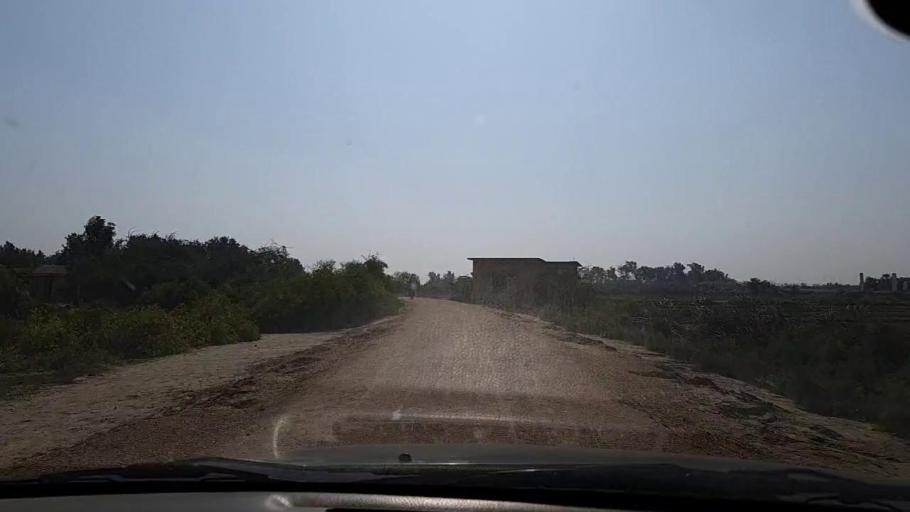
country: PK
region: Sindh
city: Chuhar Jamali
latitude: 24.3968
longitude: 67.8238
